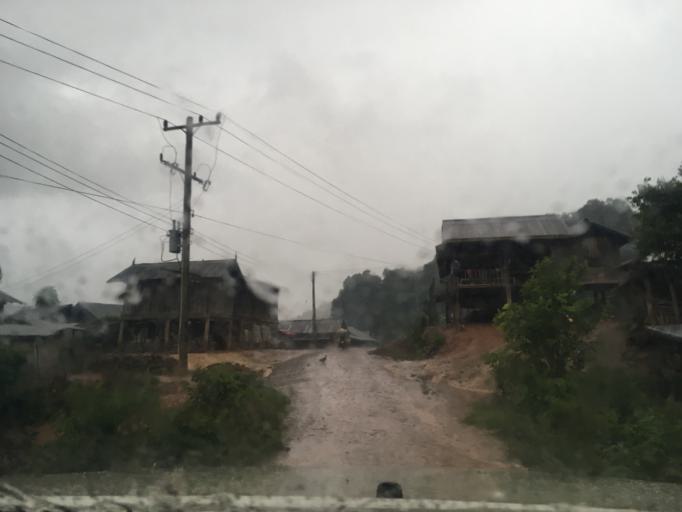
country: LA
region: Oudomxai
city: Muang La
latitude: 21.2396
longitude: 101.9547
